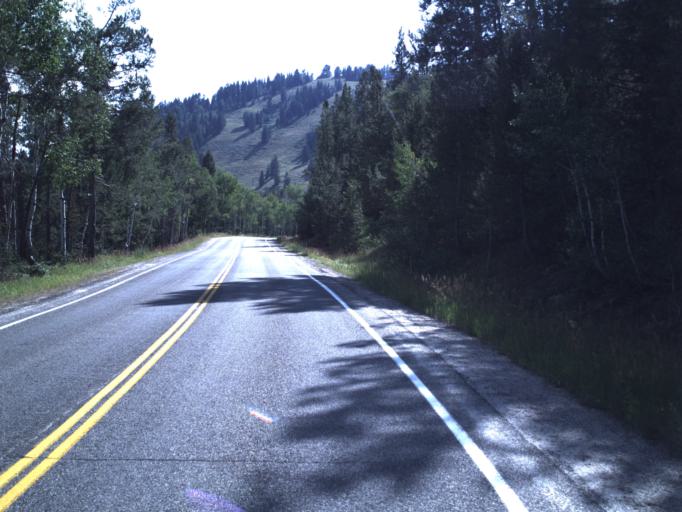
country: US
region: Utah
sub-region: Cache County
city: Richmond
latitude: 41.9733
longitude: -111.5368
